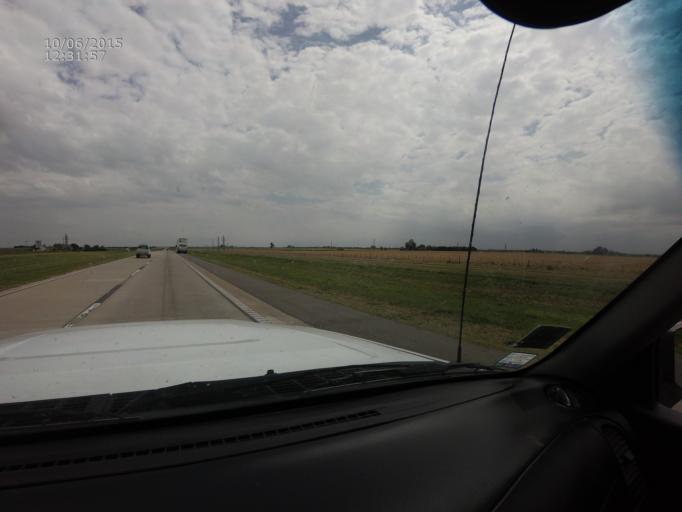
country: AR
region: Santa Fe
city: Carcarana
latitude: -32.8824
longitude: -61.1351
